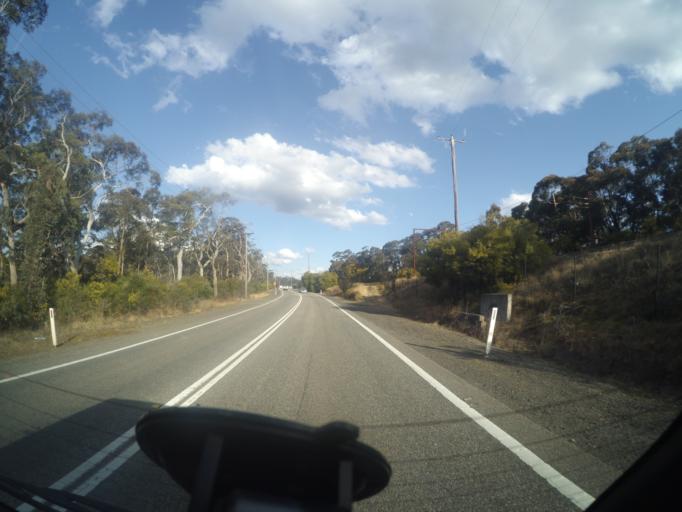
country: AU
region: New South Wales
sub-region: Blue Mountains Municipality
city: Blackheath
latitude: -33.6632
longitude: 150.2780
